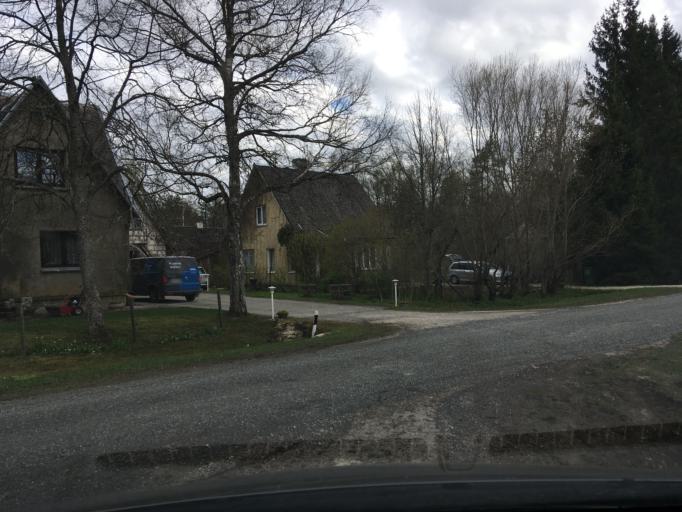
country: EE
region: Laeaene
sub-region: Lihula vald
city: Lihula
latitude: 58.6188
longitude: 23.6977
